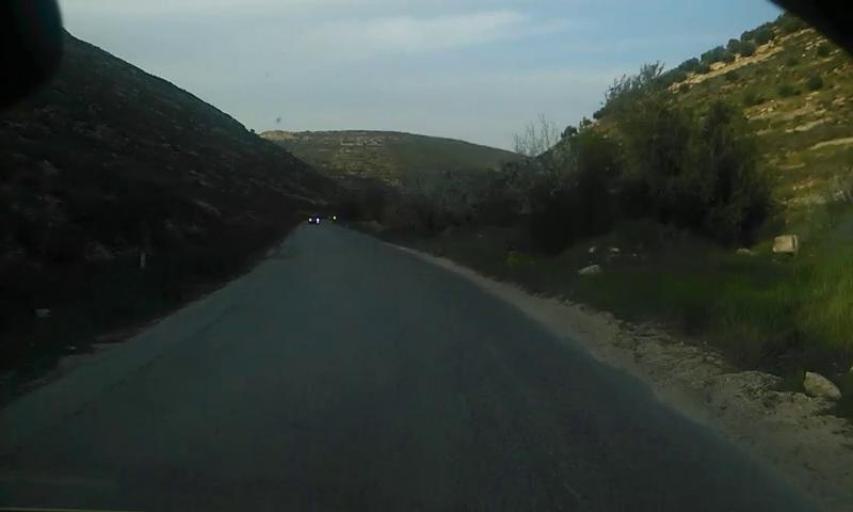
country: PS
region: West Bank
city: Ash Shuyukh
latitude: 31.5974
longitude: 35.1781
